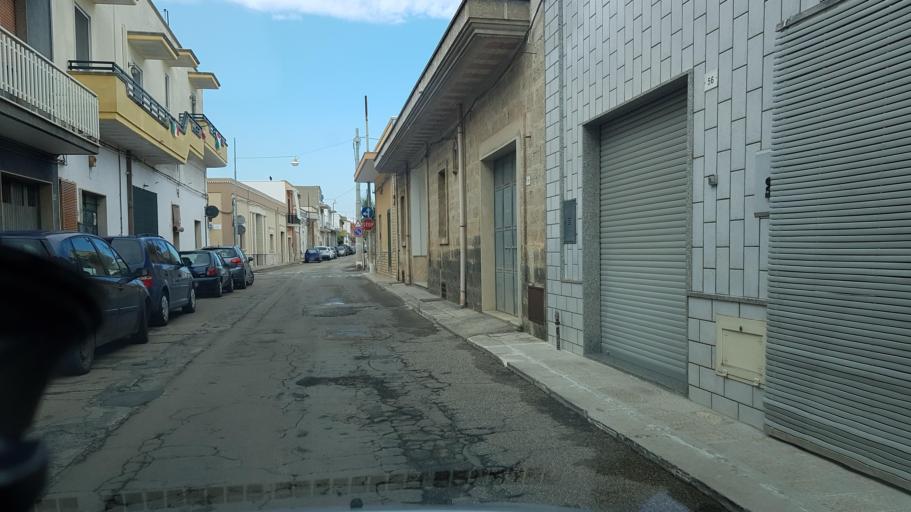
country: IT
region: Apulia
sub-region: Provincia di Brindisi
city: Torre Santa Susanna
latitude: 40.4706
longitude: 17.7408
